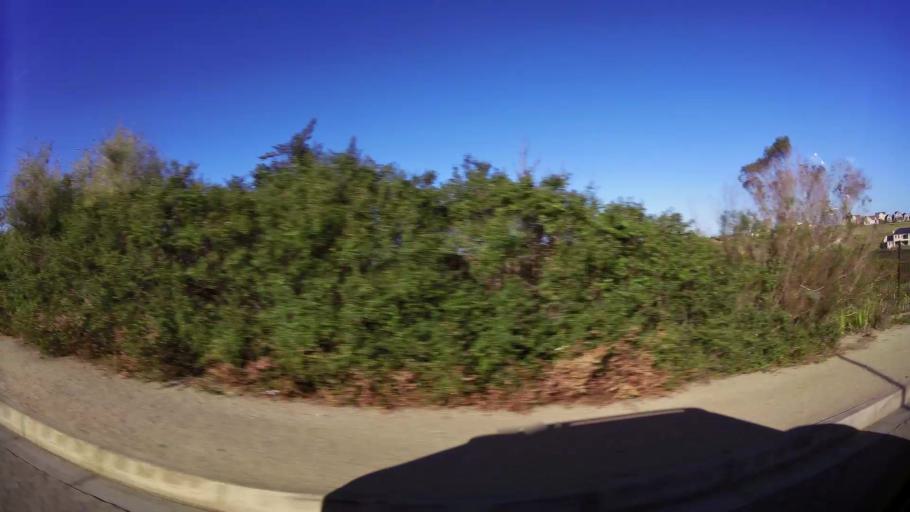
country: ZA
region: Western Cape
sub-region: Eden District Municipality
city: George
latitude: -33.9669
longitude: 22.4358
